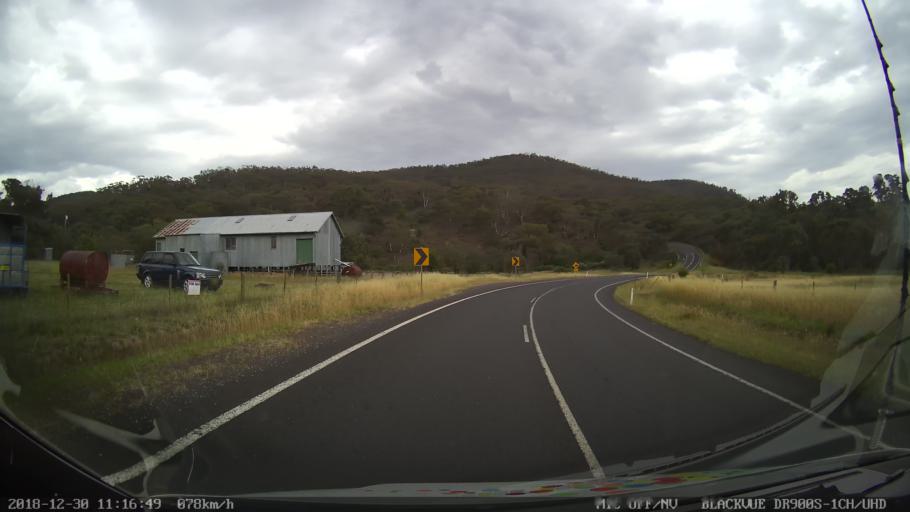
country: AU
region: New South Wales
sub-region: Snowy River
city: Jindabyne
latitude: -36.5389
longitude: 148.7024
